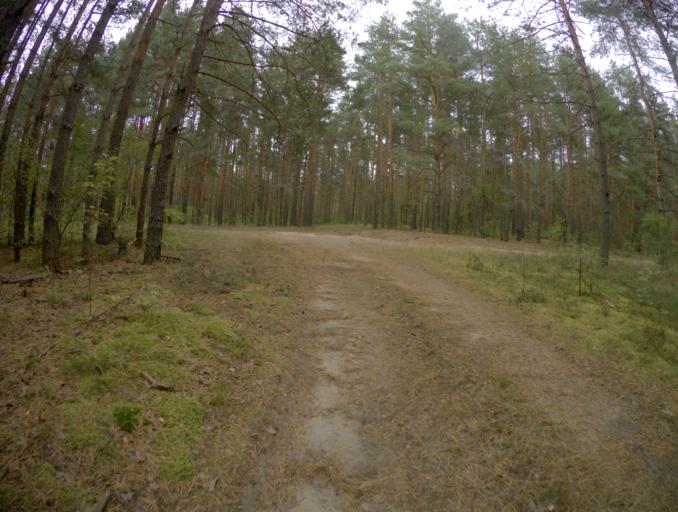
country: RU
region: Vladimir
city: Bogolyubovo
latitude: 56.1395
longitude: 40.5090
